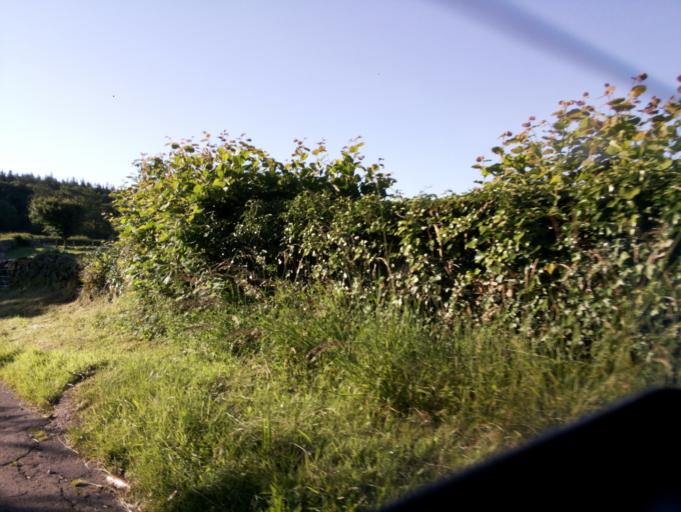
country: GB
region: Wales
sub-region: Monmouthshire
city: Llangwm
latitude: 51.6789
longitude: -2.7557
